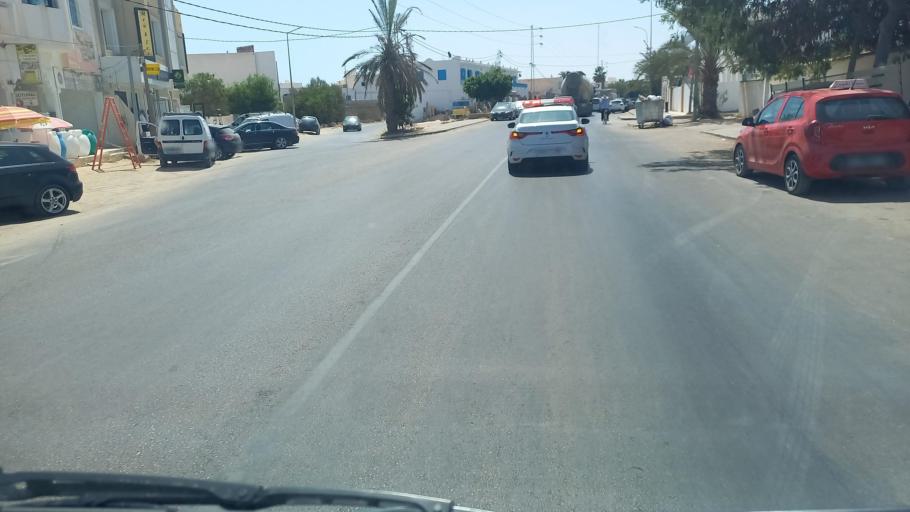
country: TN
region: Madanin
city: Houmt Souk
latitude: 33.8041
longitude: 10.8824
